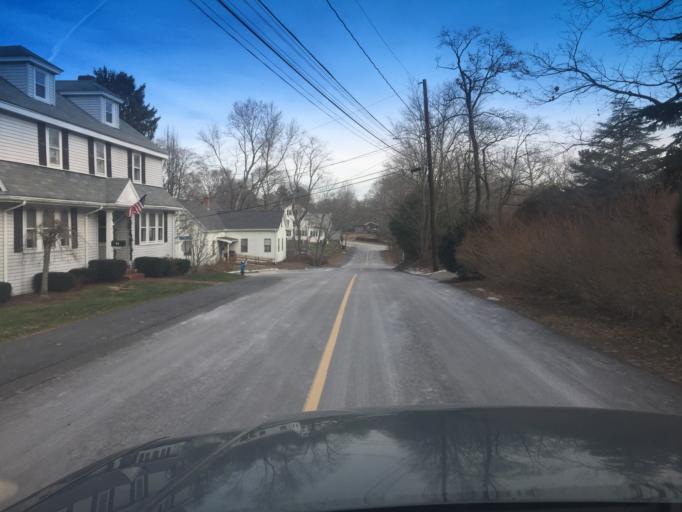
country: US
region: Massachusetts
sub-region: Norfolk County
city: Medway
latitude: 42.1426
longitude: -71.3950
